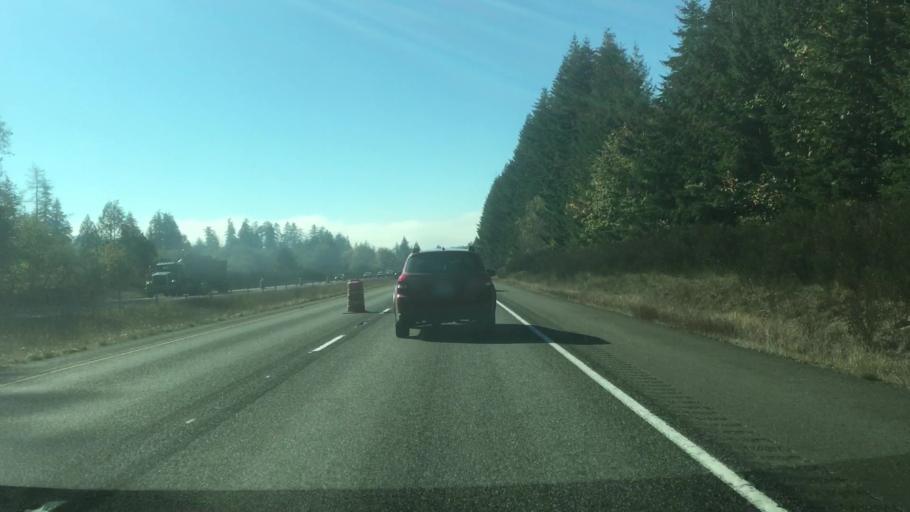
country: US
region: Washington
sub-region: Grays Harbor County
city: McCleary
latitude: 47.0519
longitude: -123.2961
